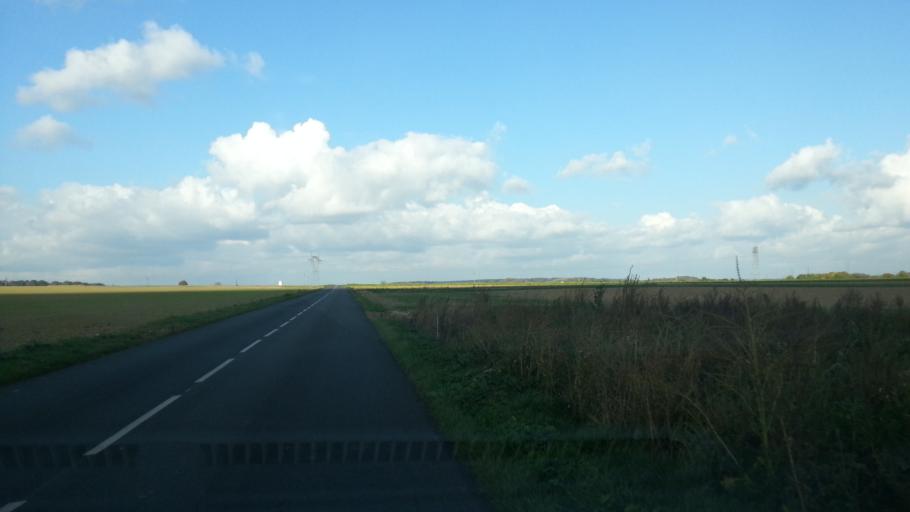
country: FR
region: Picardie
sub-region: Departement de l'Oise
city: Thiverny
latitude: 49.2410
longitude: 2.4077
